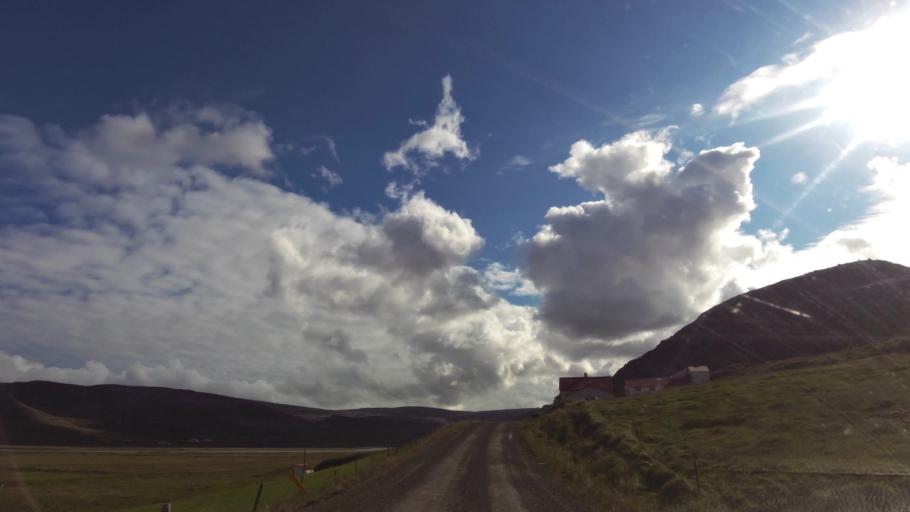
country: IS
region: West
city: Olafsvik
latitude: 65.5774
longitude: -24.1508
